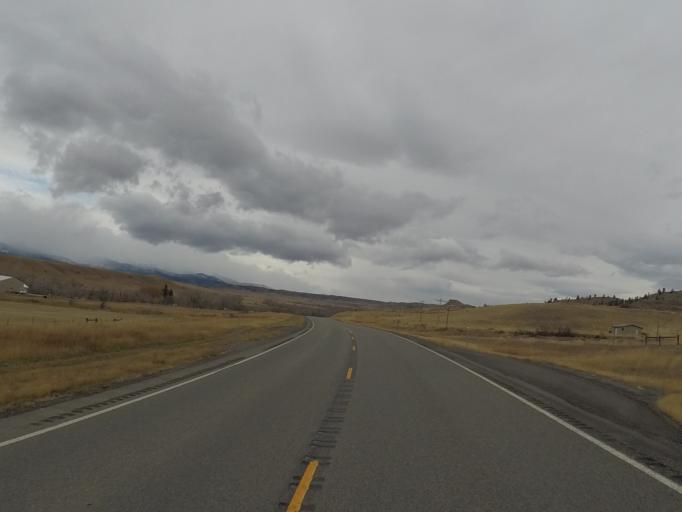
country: US
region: Montana
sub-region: Sweet Grass County
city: Big Timber
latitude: 45.9236
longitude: -109.9802
